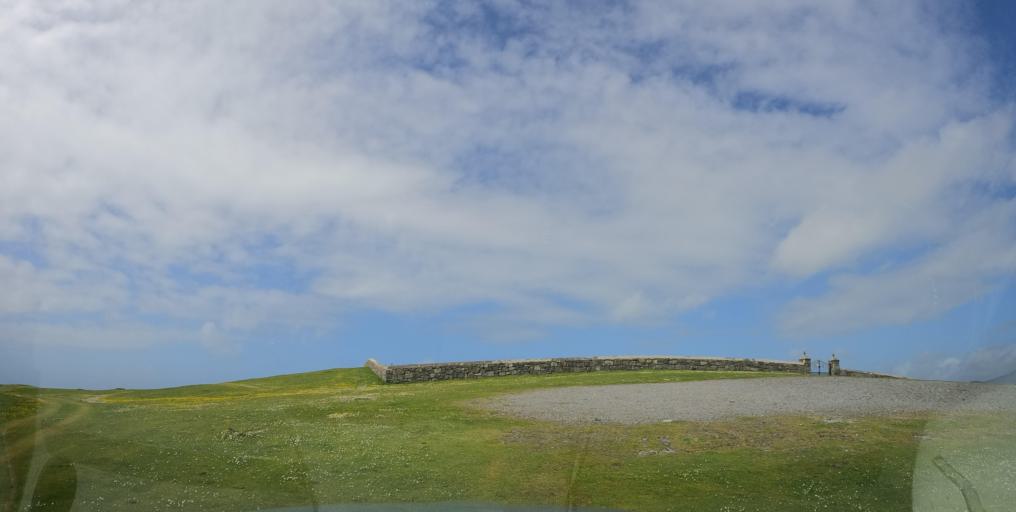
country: GB
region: Scotland
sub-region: Eilean Siar
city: Isle of South Uist
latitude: 57.1703
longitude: -7.4039
